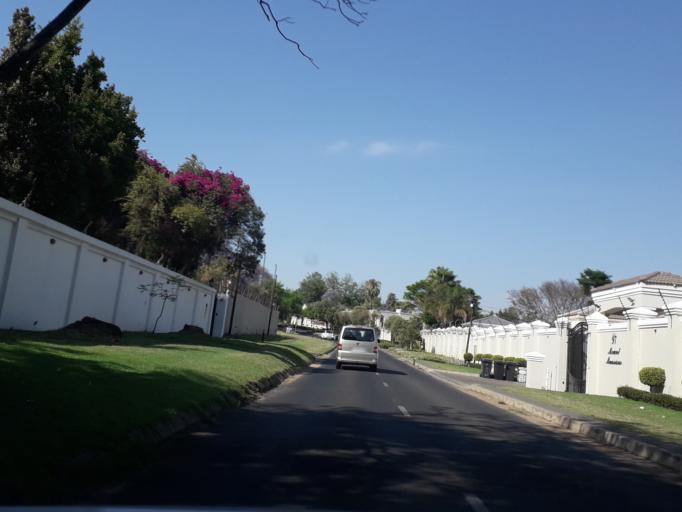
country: ZA
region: Gauteng
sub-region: City of Johannesburg Metropolitan Municipality
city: Midrand
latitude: -26.0450
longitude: 28.0322
